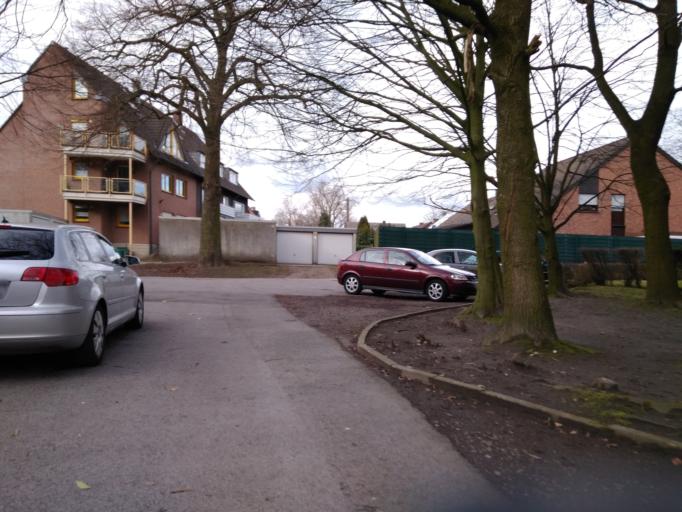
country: DE
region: North Rhine-Westphalia
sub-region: Regierungsbezirk Munster
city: Gladbeck
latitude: 51.5843
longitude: 7.0278
